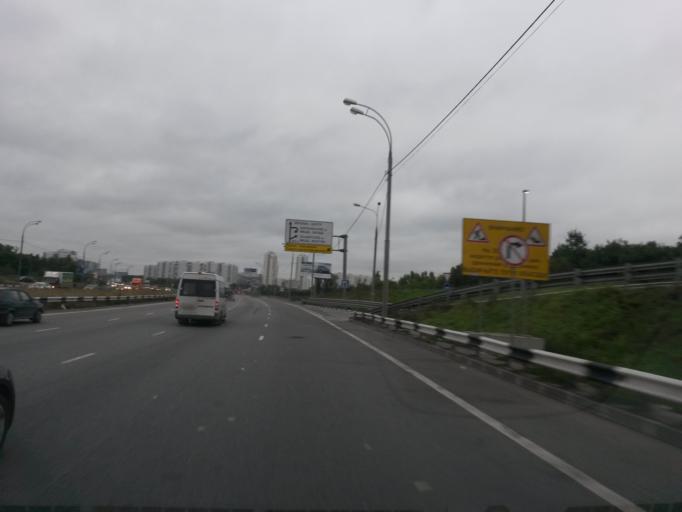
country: RU
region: Moscow
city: Biryulevo
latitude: 55.5706
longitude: 37.6928
